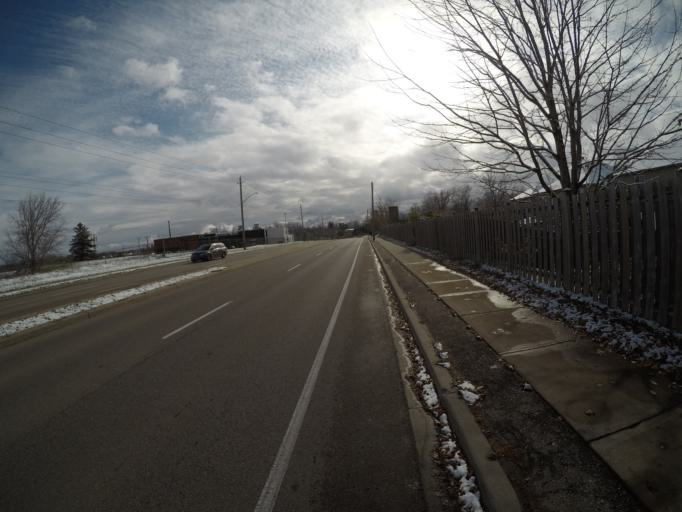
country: CA
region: Ontario
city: Waterloo
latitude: 43.4972
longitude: -80.4916
